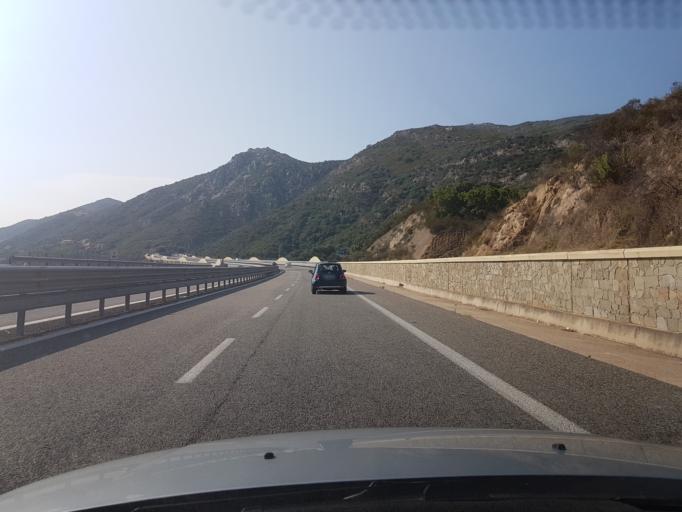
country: IT
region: Sardinia
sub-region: Provincia di Olbia-Tempio
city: San Teodoro
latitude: 40.7931
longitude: 9.6100
